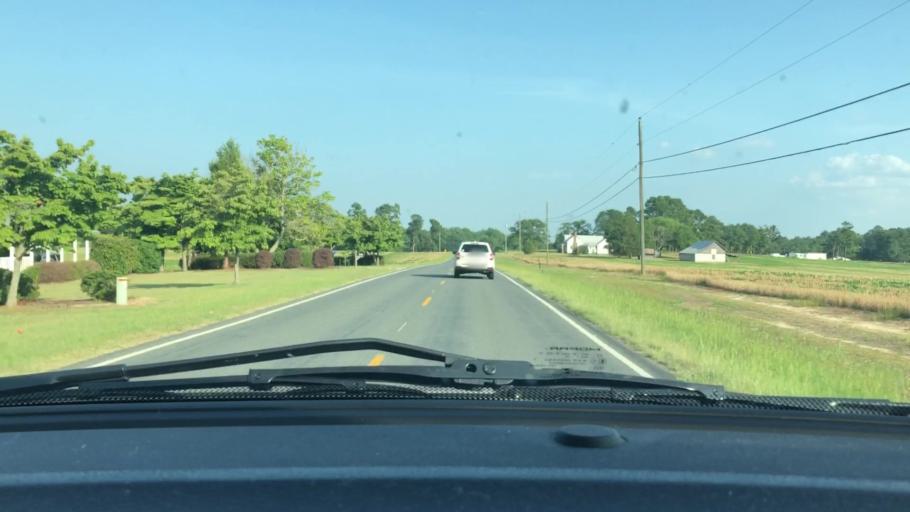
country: US
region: North Carolina
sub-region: Lee County
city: Broadway
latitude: 35.3667
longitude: -79.0943
